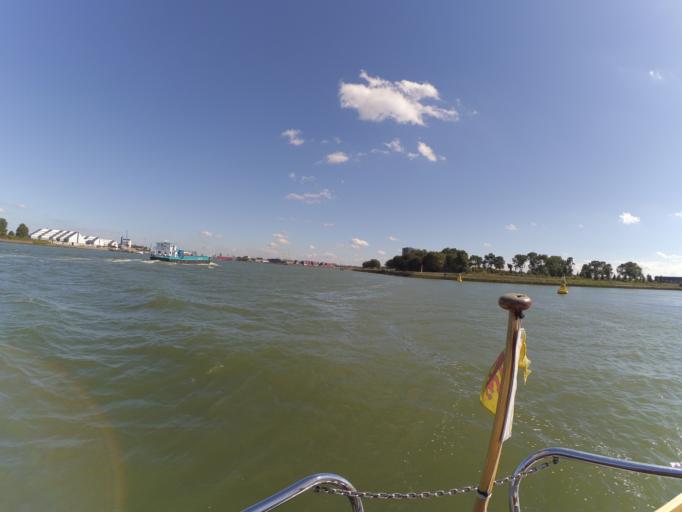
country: NL
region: South Holland
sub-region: Gemeente Schiedam
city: Schiedam
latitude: 51.8957
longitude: 4.3826
